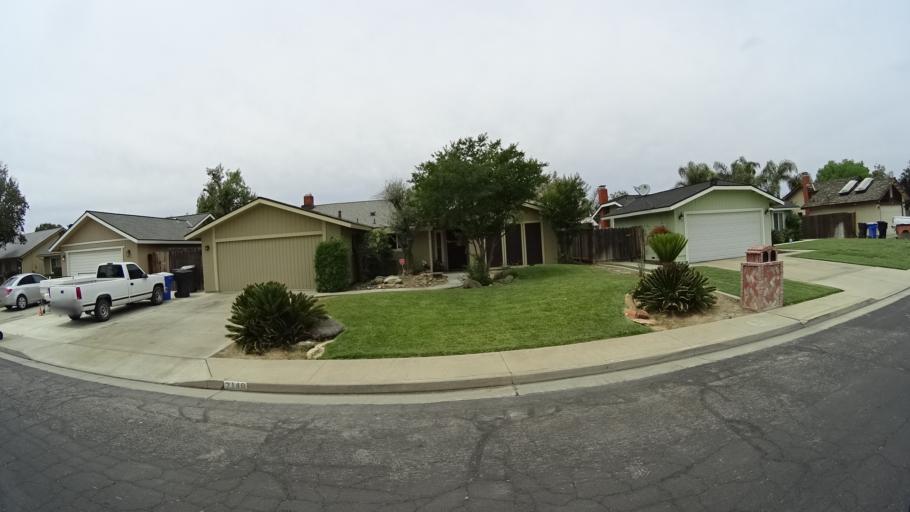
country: US
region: California
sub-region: Kings County
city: Hanford
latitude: 36.3508
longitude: -119.6351
